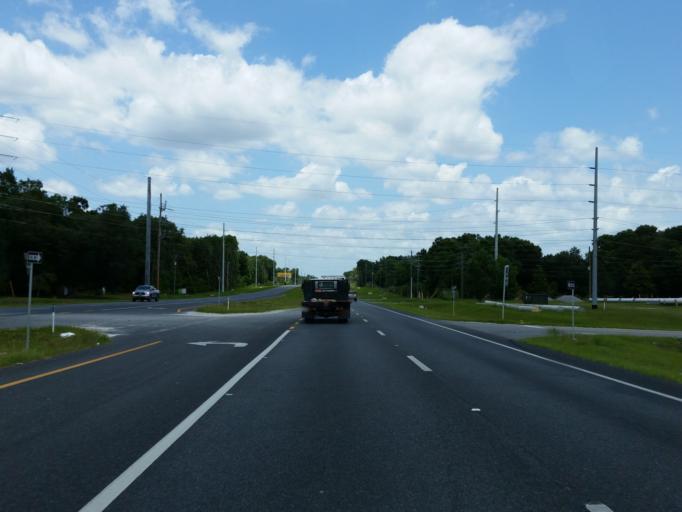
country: US
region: Florida
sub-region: Marion County
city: Belleview
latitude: 28.9696
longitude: -82.0411
